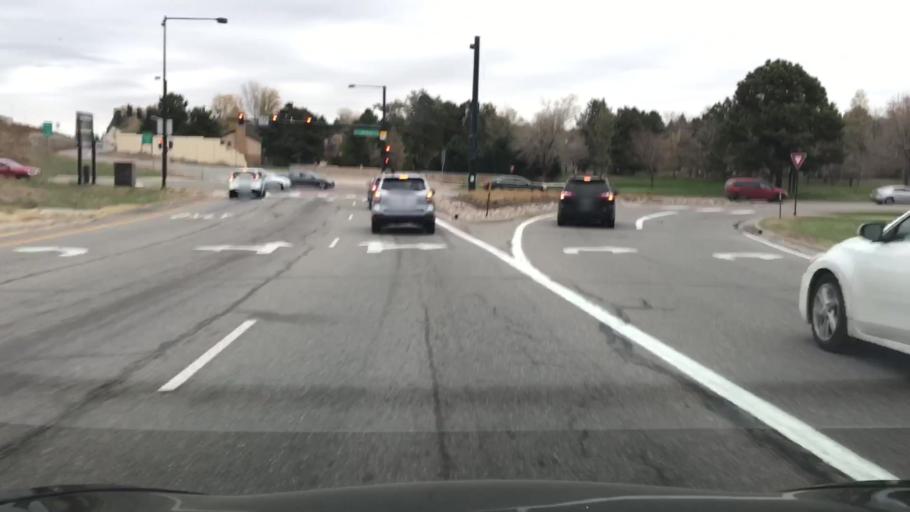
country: US
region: Colorado
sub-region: Arapahoe County
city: Castlewood
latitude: 39.6347
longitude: -104.8942
